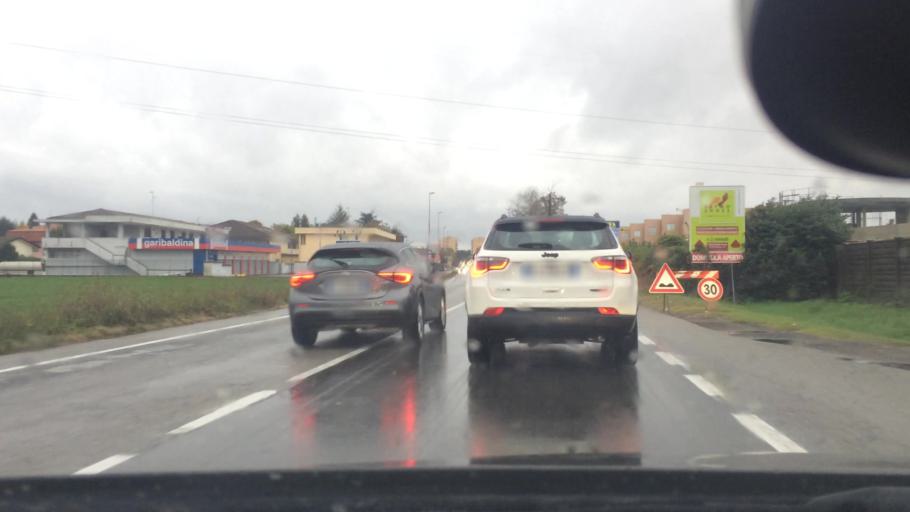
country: IT
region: Lombardy
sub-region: Citta metropolitana di Milano
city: Pogliano Milanese
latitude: 45.5456
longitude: 8.9989
